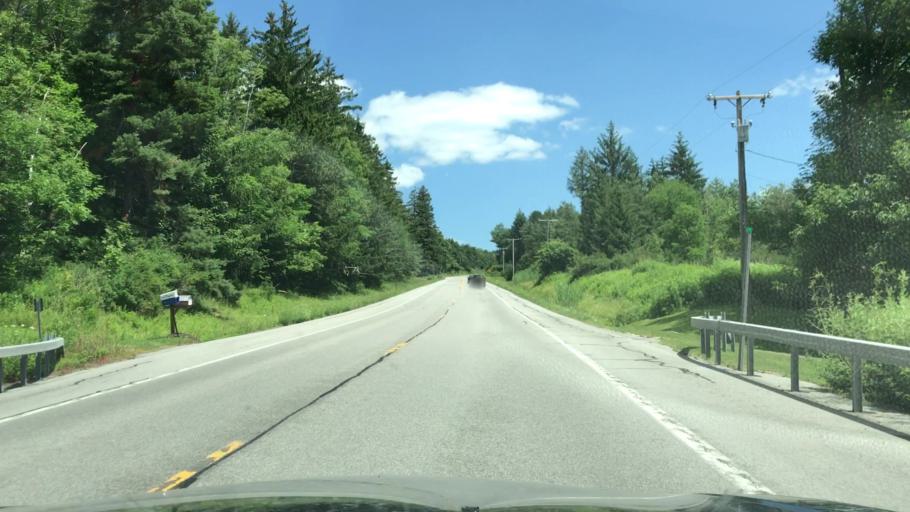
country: US
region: New York
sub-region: Wyoming County
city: Warsaw
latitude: 42.7491
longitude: -78.2424
